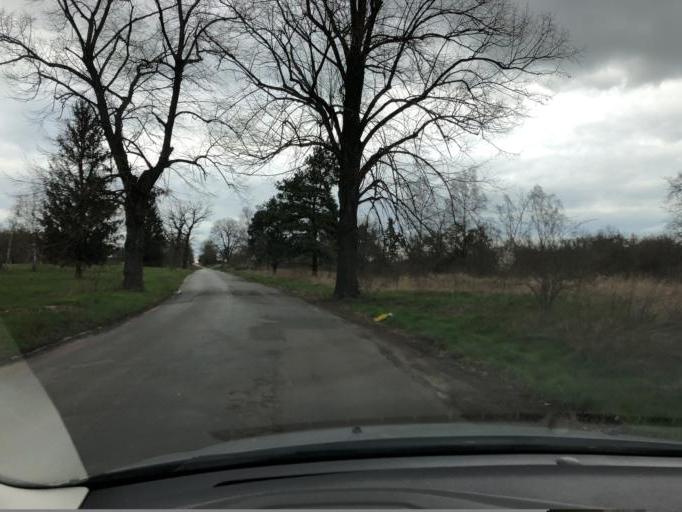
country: DE
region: Saxony-Anhalt
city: Muschwitz
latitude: 51.1715
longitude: 12.1399
